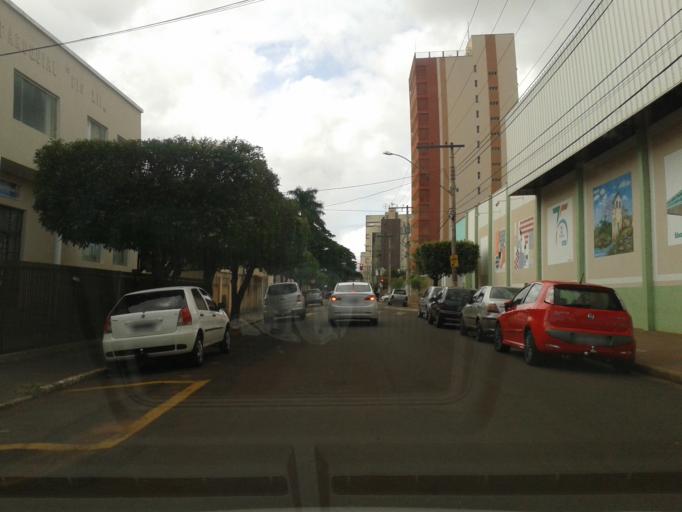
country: BR
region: Minas Gerais
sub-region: Ituiutaba
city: Ituiutaba
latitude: -18.9685
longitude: -49.4649
